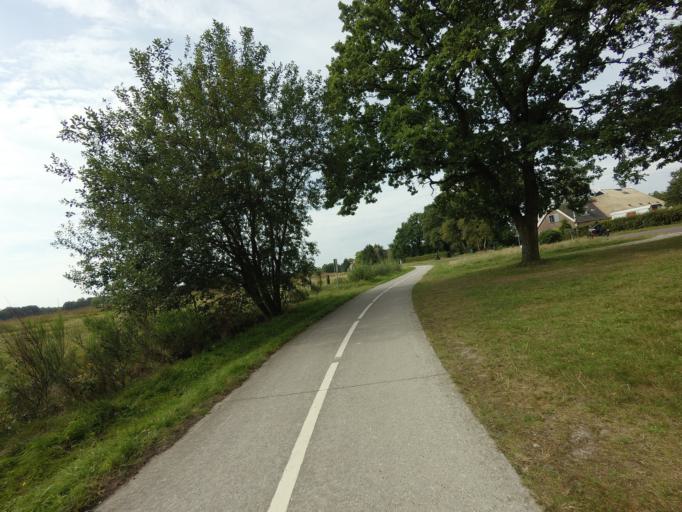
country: NL
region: Drenthe
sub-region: Gemeente Westerveld
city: Dwingeloo
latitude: 52.9053
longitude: 6.2899
